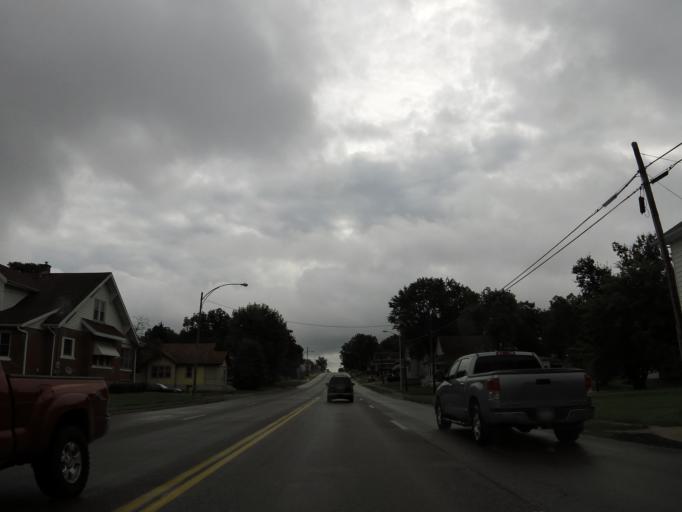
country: US
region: Missouri
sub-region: Cape Girardeau County
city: Cape Girardeau
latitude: 37.3018
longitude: -89.5350
